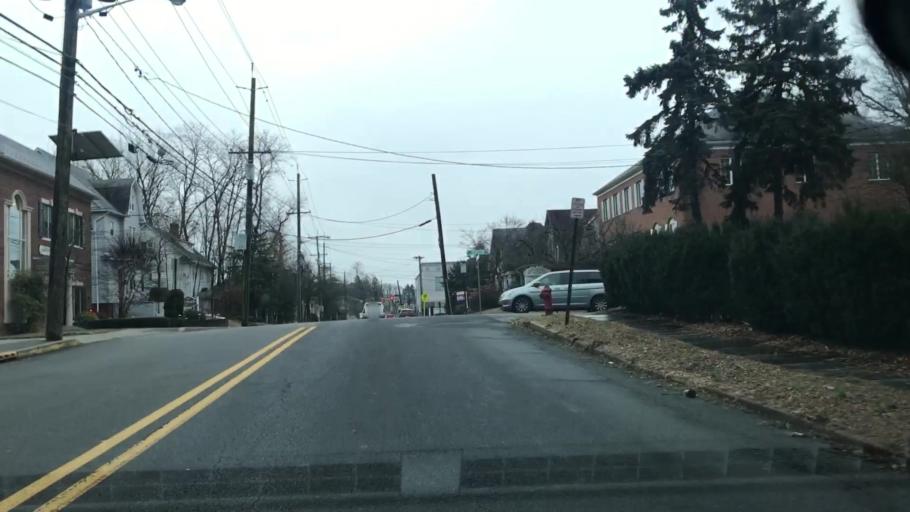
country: US
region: New Jersey
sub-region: Bergen County
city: Westwood
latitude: 40.9947
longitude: -74.0309
